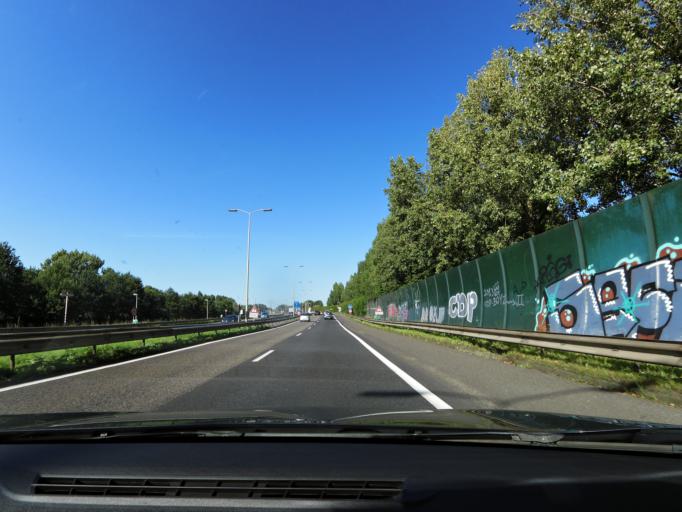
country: NL
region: South Holland
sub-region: Gemeente Papendrecht
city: Papendrecht
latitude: 51.8098
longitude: 4.7046
